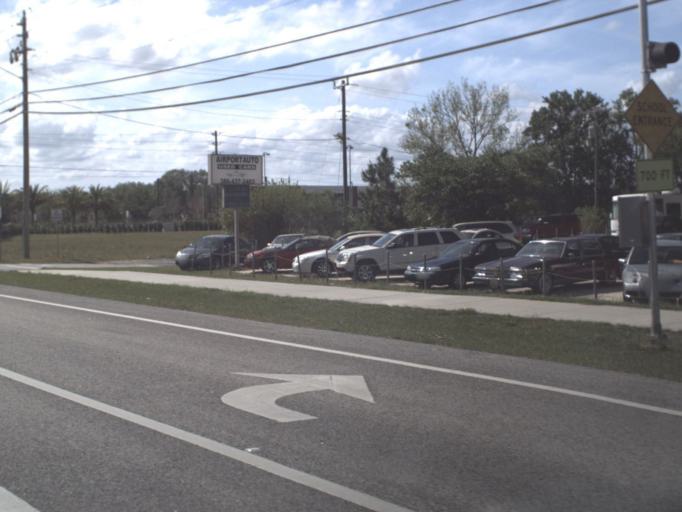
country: US
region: Florida
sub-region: Flagler County
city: Bunnell
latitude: 29.4756
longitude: -81.2057
